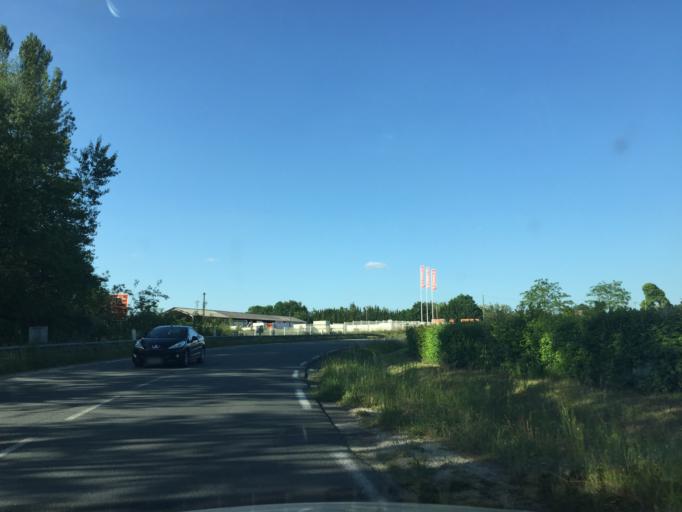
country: FR
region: Aquitaine
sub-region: Departement de la Dordogne
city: La Roche-Chalais
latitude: 45.1632
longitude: 0.0082
